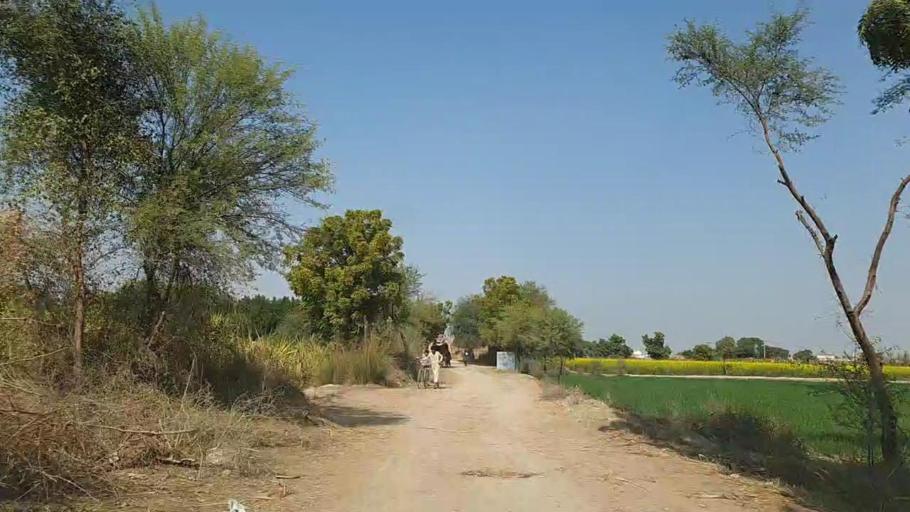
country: PK
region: Sindh
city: Daur
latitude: 26.4987
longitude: 68.2719
